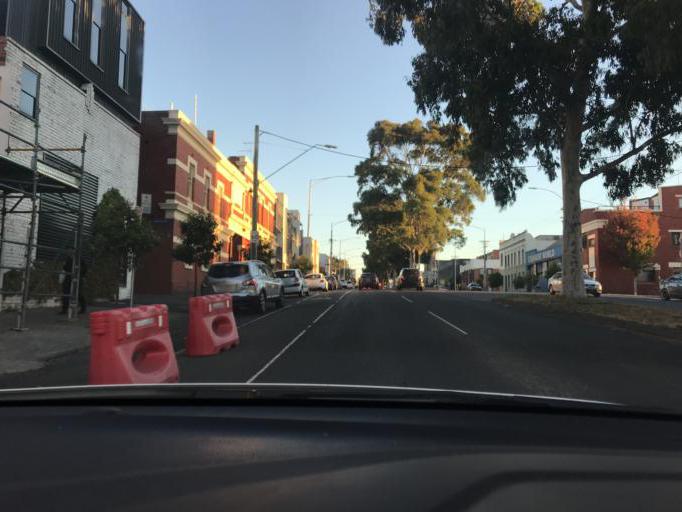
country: AU
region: Victoria
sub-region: Melbourne
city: North Melbourne
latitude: -37.8009
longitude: 144.9486
